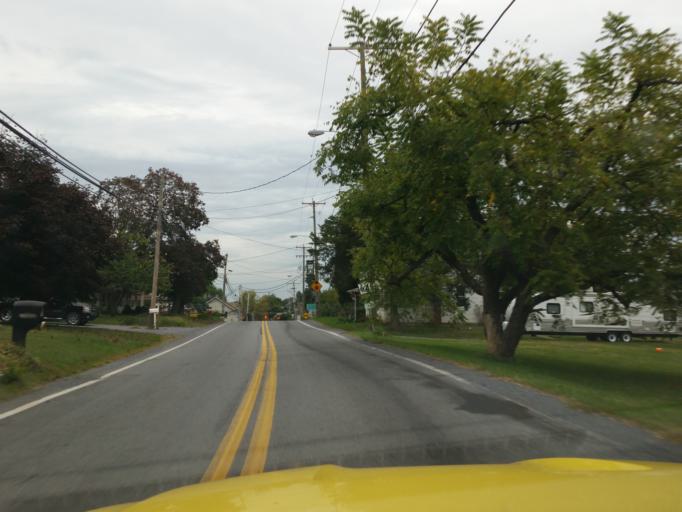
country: US
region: Pennsylvania
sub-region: Lebanon County
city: Myerstown
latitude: 40.4498
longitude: -76.3368
